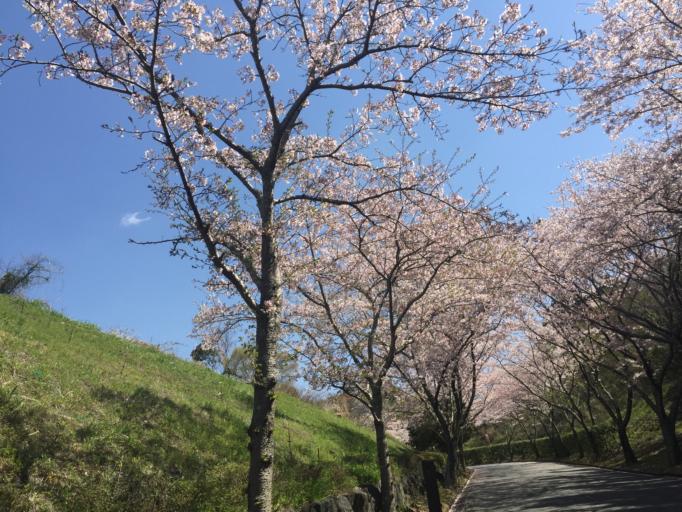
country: JP
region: Shizuoka
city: Kanaya
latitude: 34.7892
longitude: 138.1178
